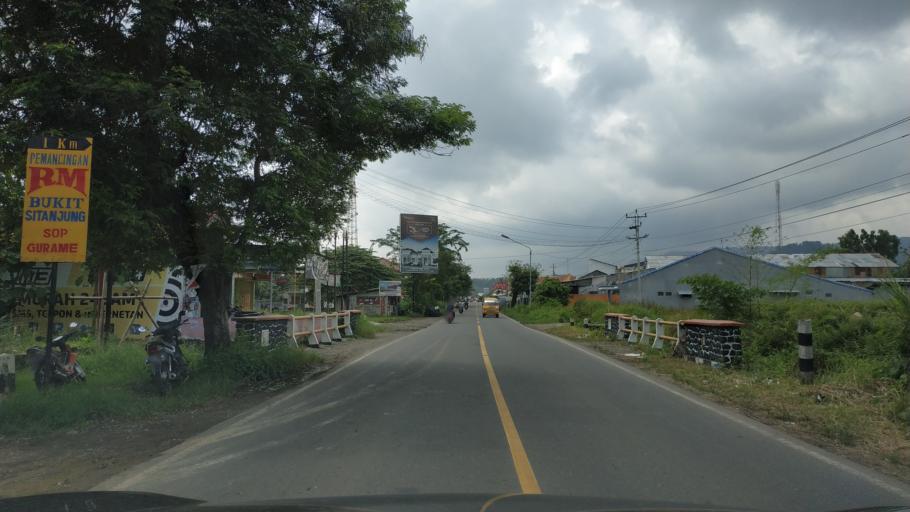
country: ID
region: Central Java
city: Lebaksiu
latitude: -7.0460
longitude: 109.1377
